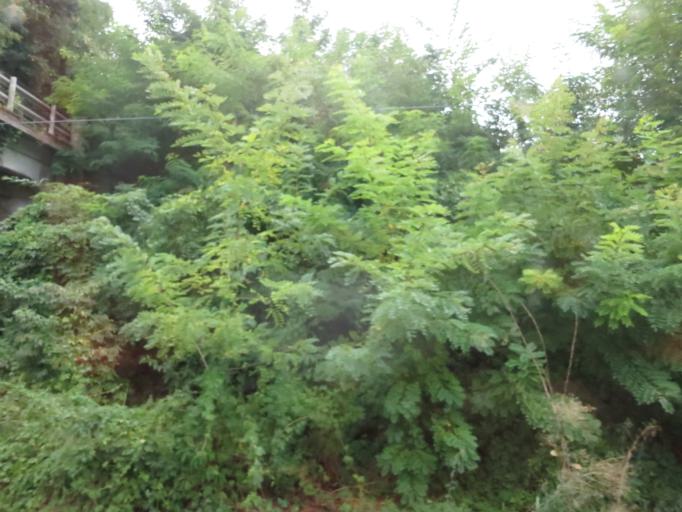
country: IT
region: Lombardy
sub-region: Provincia di Como
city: Carimate
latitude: 45.7128
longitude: 9.0979
